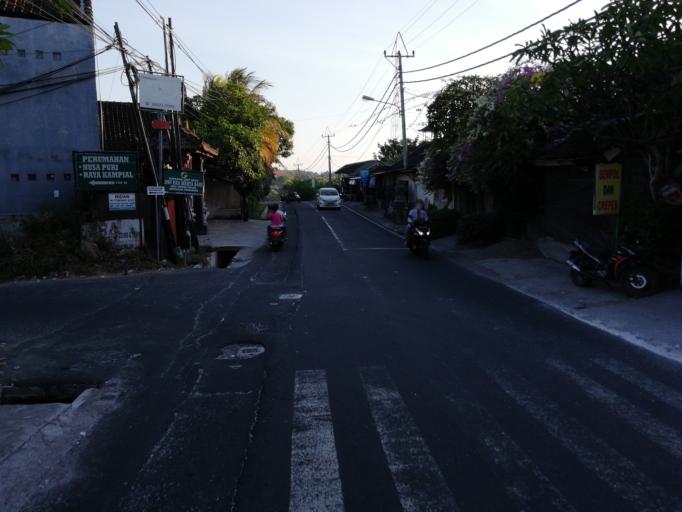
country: ID
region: Bali
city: Bualu
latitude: -8.8198
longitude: 115.1893
